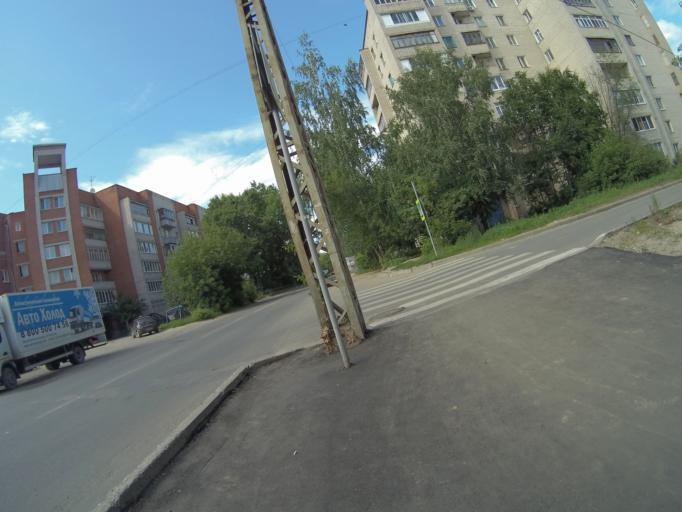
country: RU
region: Vladimir
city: Vladimir
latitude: 56.1224
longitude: 40.3707
